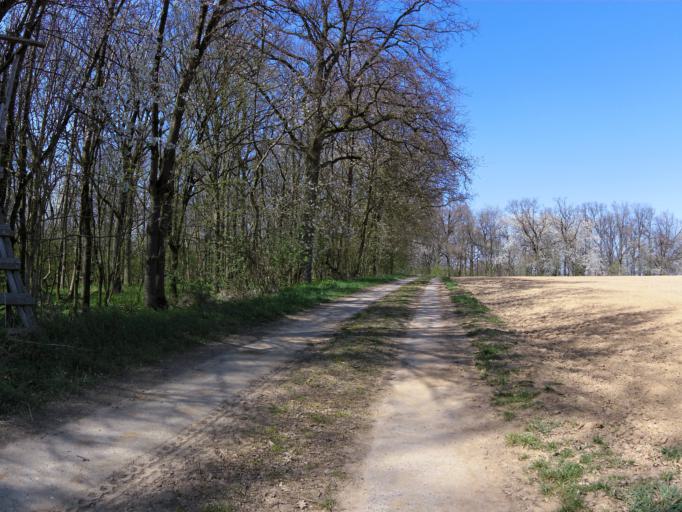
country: DE
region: Bavaria
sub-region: Regierungsbezirk Unterfranken
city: Rottendorf
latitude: 49.8141
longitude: 10.0669
